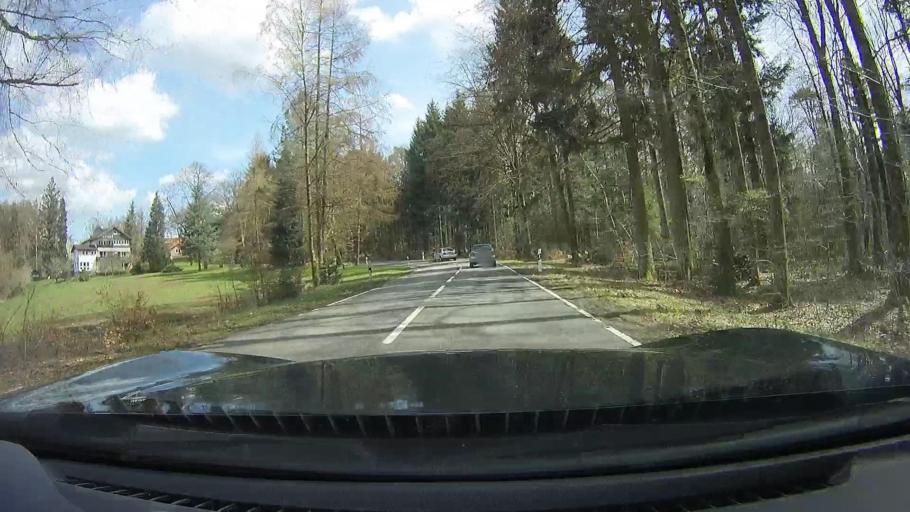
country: DE
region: Hesse
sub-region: Regierungsbezirk Darmstadt
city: Beerfelden
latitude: 49.5760
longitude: 9.0174
